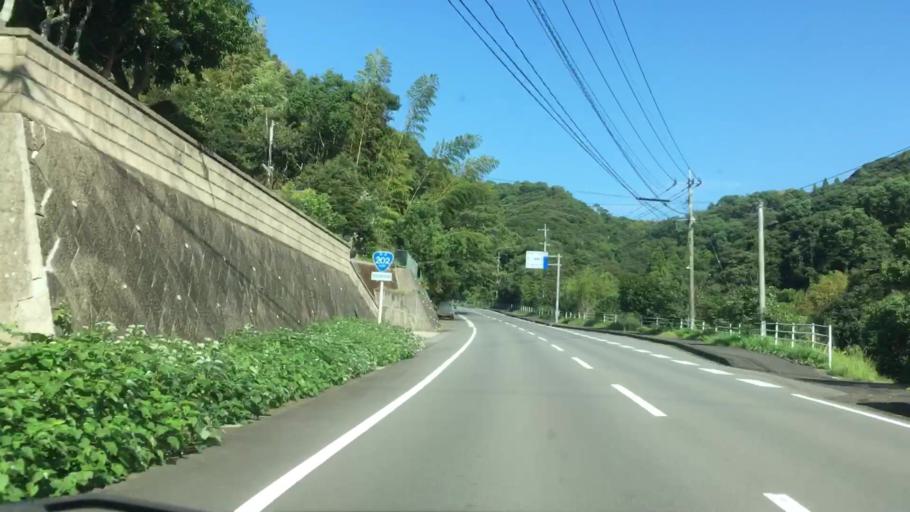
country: JP
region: Nagasaki
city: Sasebo
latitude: 33.0026
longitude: 129.6611
